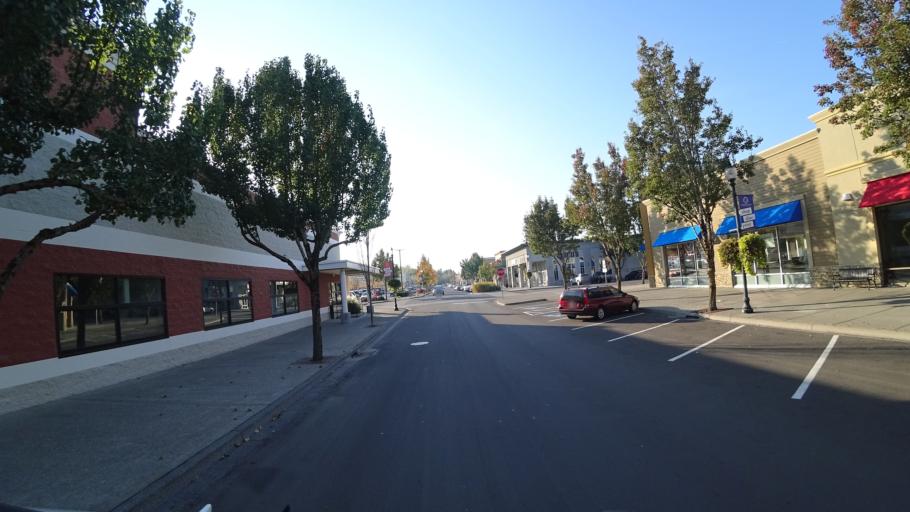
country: US
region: Oregon
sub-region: Multnomah County
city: Gresham
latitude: 45.5059
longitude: -122.4374
